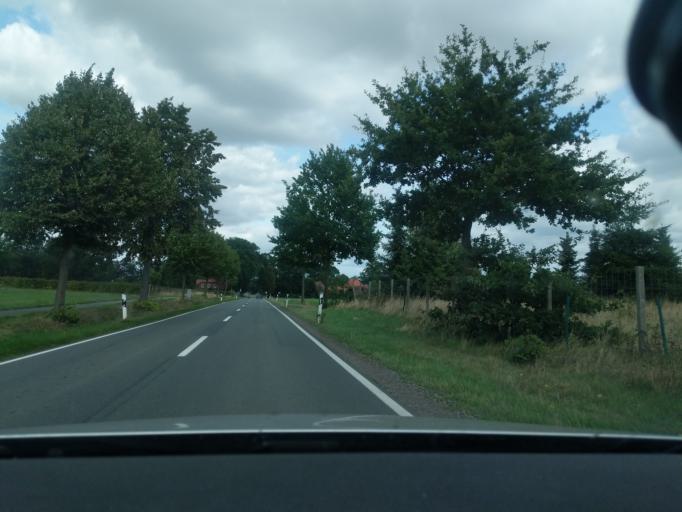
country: DE
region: Lower Saxony
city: Warpe
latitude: 52.7556
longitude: 9.0821
